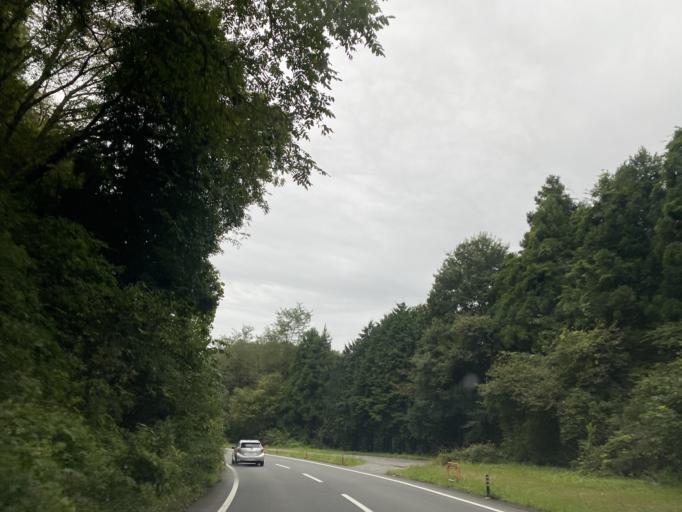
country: JP
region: Fukushima
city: Sukagawa
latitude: 37.2987
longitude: 140.2482
